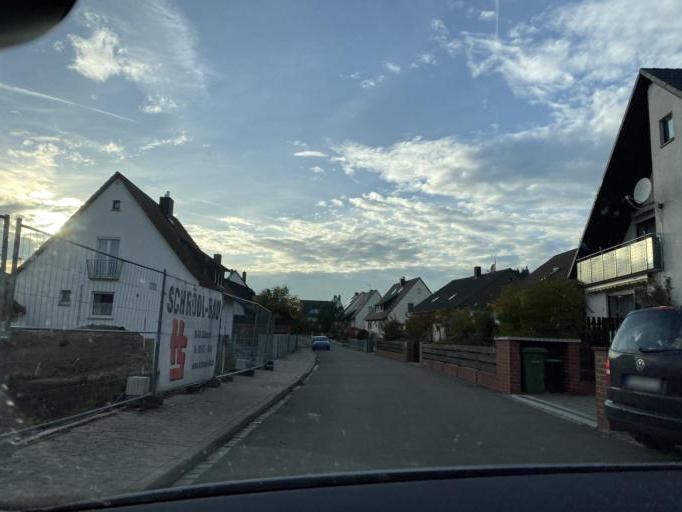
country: DE
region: Bavaria
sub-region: Regierungsbezirk Mittelfranken
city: Puschendorf
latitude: 49.5253
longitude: 10.8332
